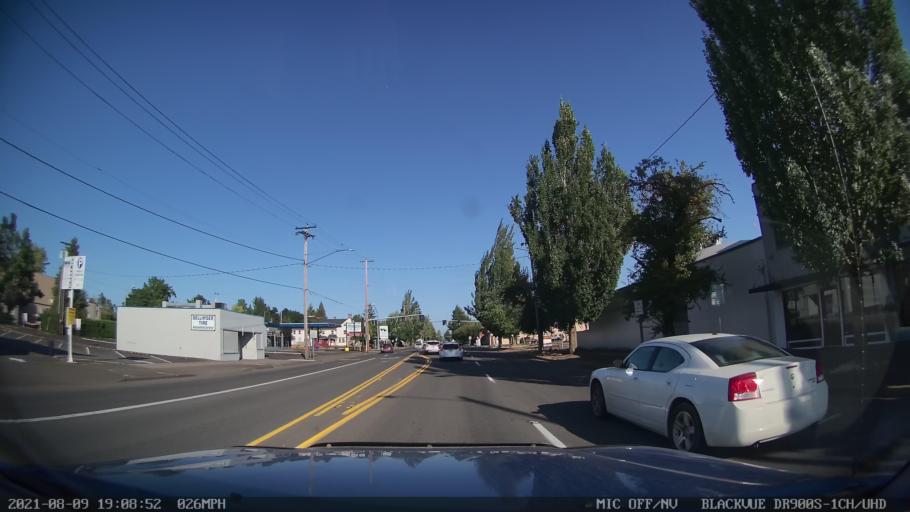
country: US
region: Oregon
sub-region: Marion County
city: Salem
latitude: 44.9366
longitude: -123.0256
